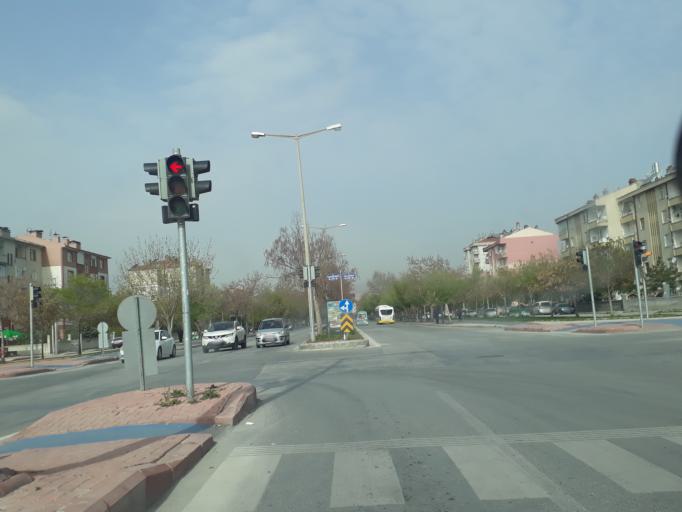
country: TR
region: Konya
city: Selcuklu
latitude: 37.9372
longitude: 32.4992
